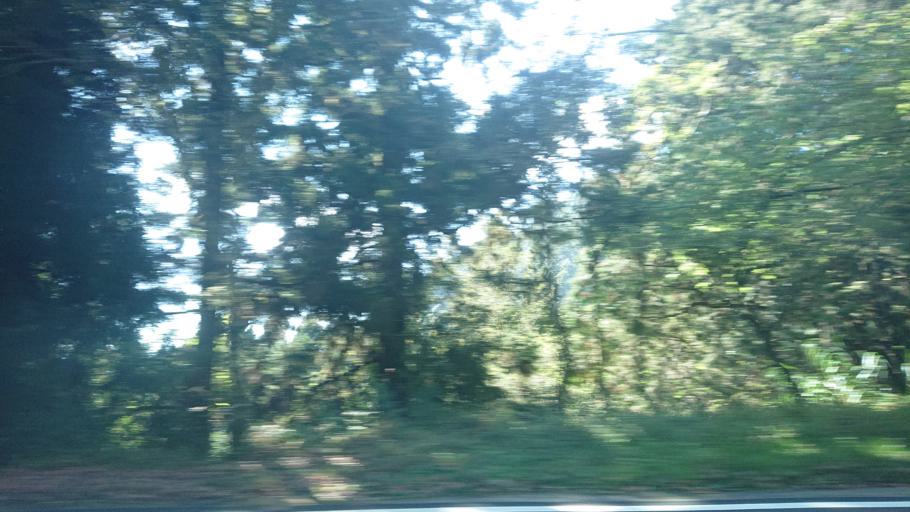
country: TW
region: Taiwan
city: Lugu
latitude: 23.5050
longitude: 120.8196
